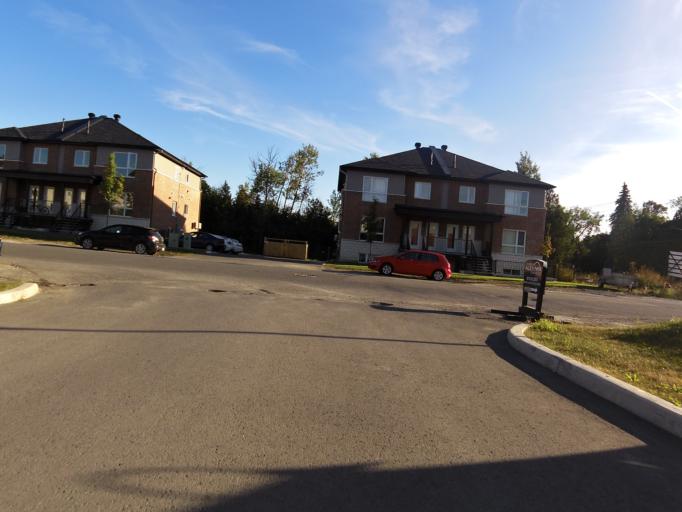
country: CA
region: Ontario
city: Bells Corners
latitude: 45.4228
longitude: -75.8507
